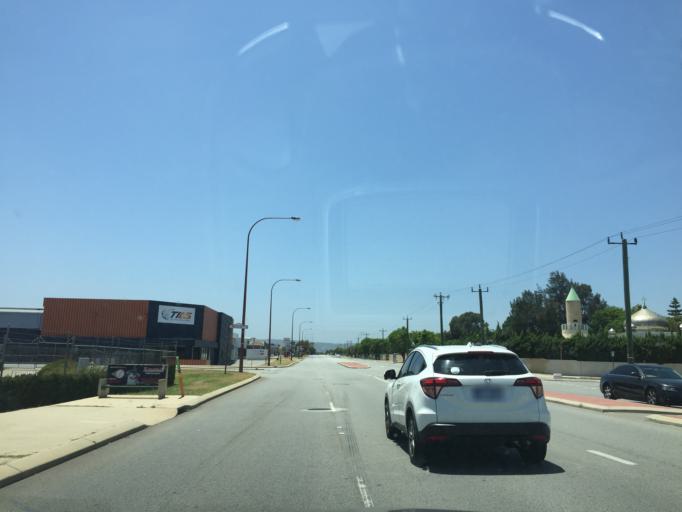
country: AU
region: Western Australia
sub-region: Canning
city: Queens Park
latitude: -31.9969
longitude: 115.9467
